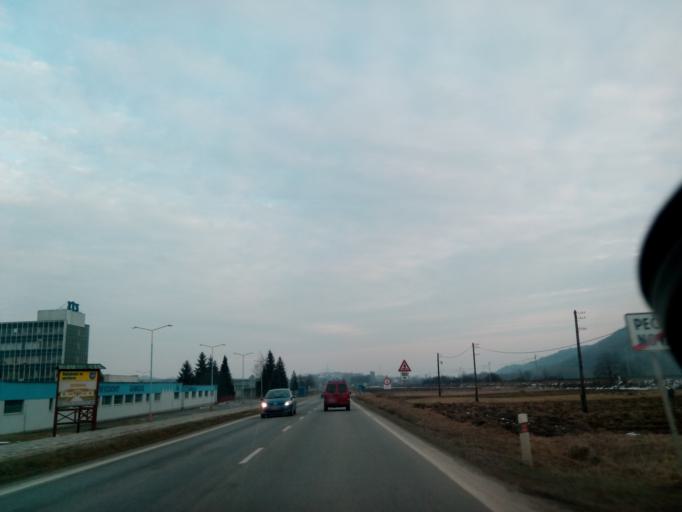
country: SK
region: Presovsky
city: Sabinov
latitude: 49.1196
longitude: 21.0567
